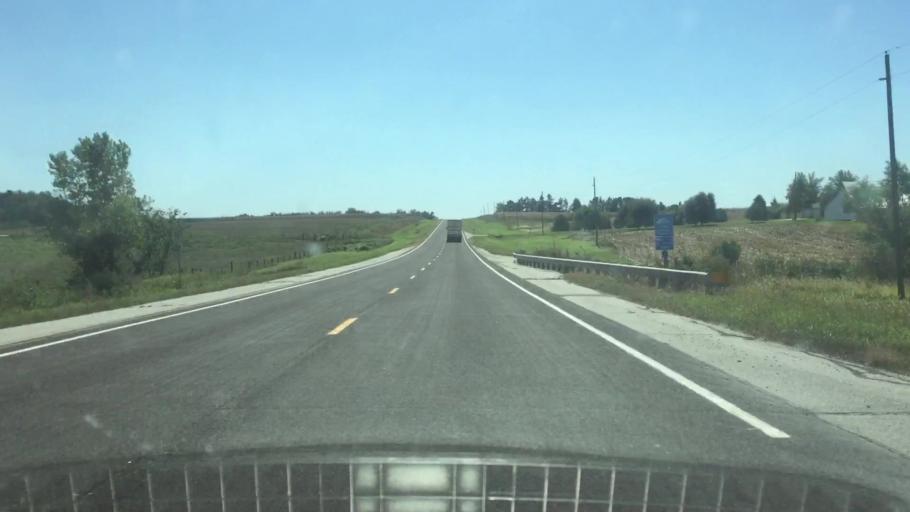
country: US
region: Nebraska
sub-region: Gage County
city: Wymore
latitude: 40.0301
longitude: -96.6523
